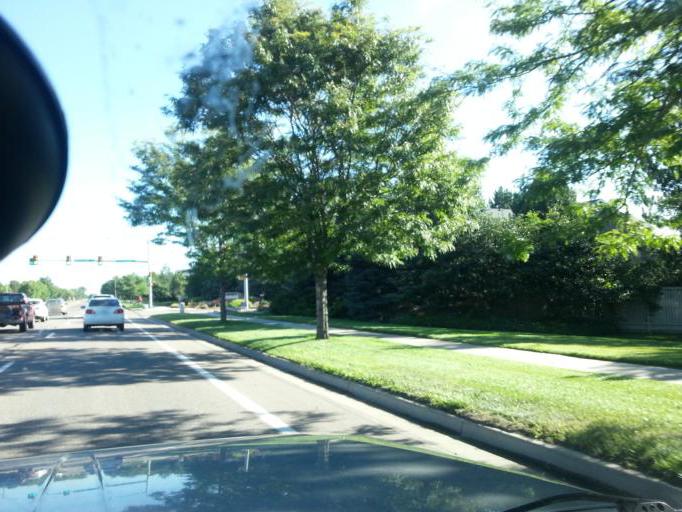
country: US
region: Colorado
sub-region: Larimer County
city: Fort Collins
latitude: 40.5143
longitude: -105.0393
